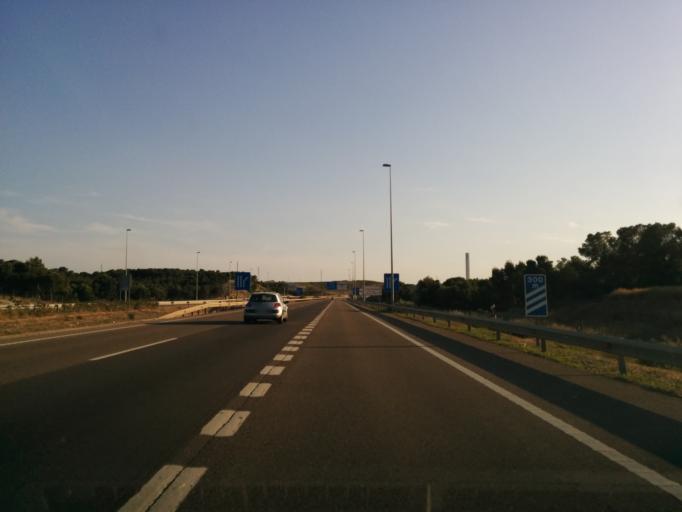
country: ES
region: Aragon
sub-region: Provincia de Zaragoza
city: Zaragoza
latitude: 41.6132
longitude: -0.8720
